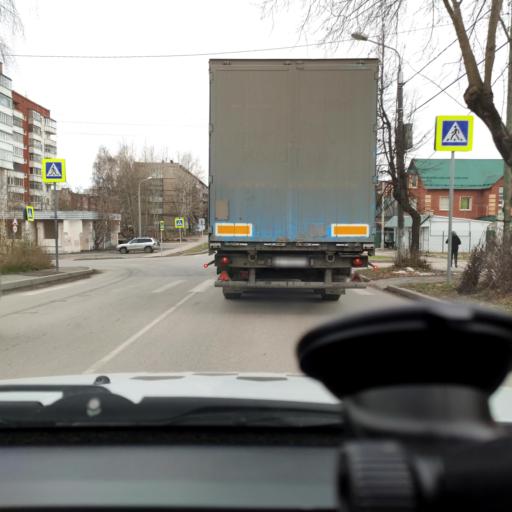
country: RU
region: Perm
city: Perm
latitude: 58.1079
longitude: 56.2968
